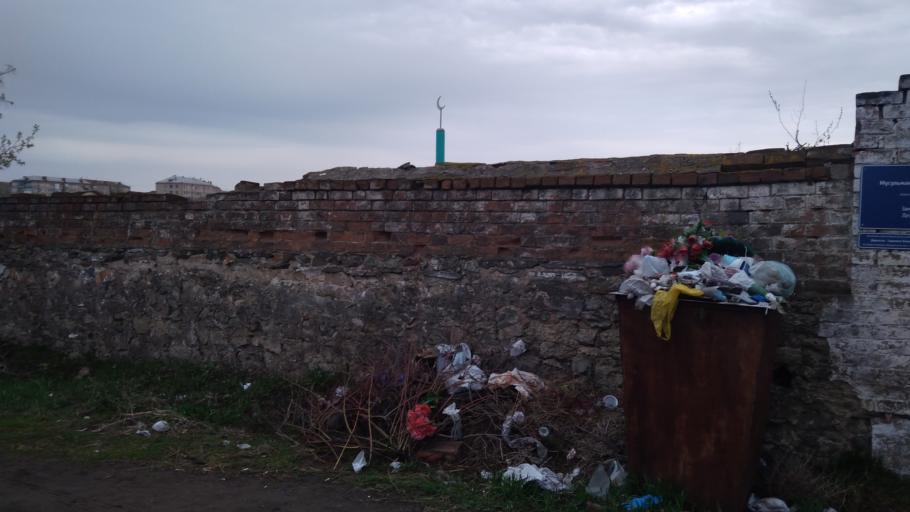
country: RU
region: Chelyabinsk
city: Troitsk
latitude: 54.0830
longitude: 61.5264
